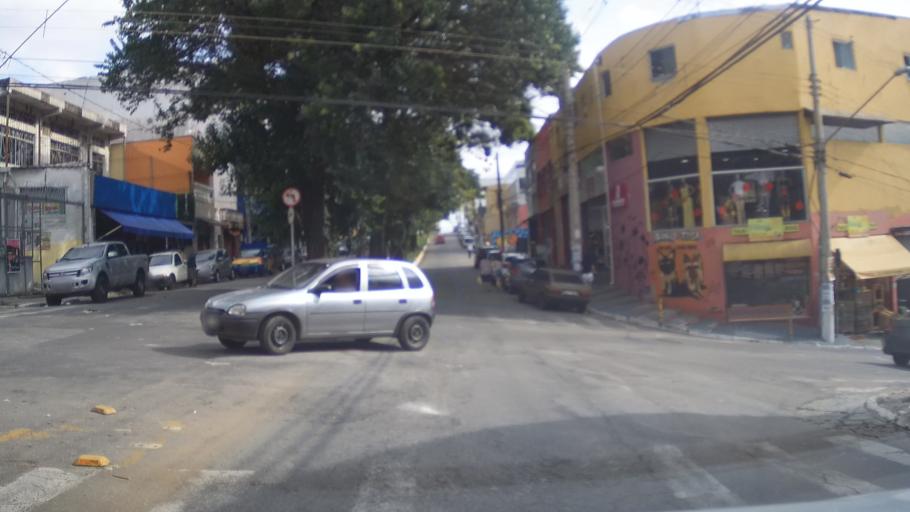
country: BR
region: Sao Paulo
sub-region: Guarulhos
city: Guarulhos
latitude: -23.4112
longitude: -46.4541
